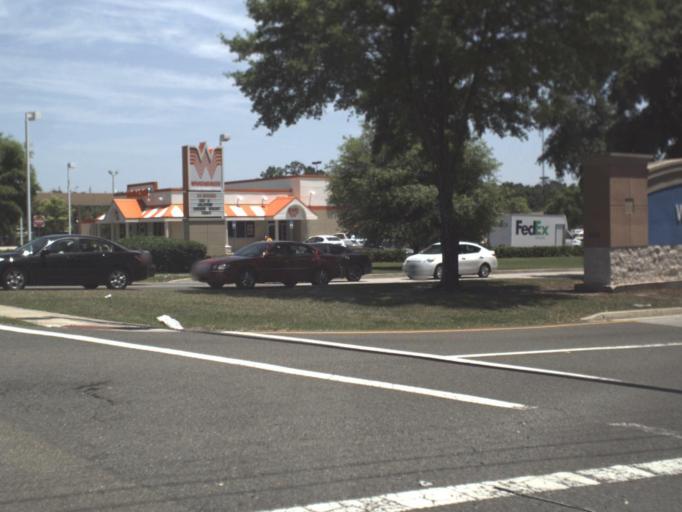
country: US
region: Florida
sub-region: Duval County
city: Jacksonville
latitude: 30.2869
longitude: -81.5642
